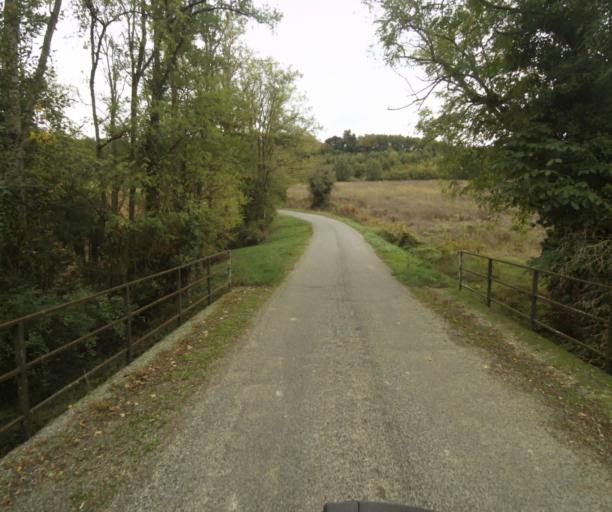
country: FR
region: Midi-Pyrenees
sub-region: Departement du Tarn-et-Garonne
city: Verdun-sur-Garonne
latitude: 43.8458
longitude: 1.1177
